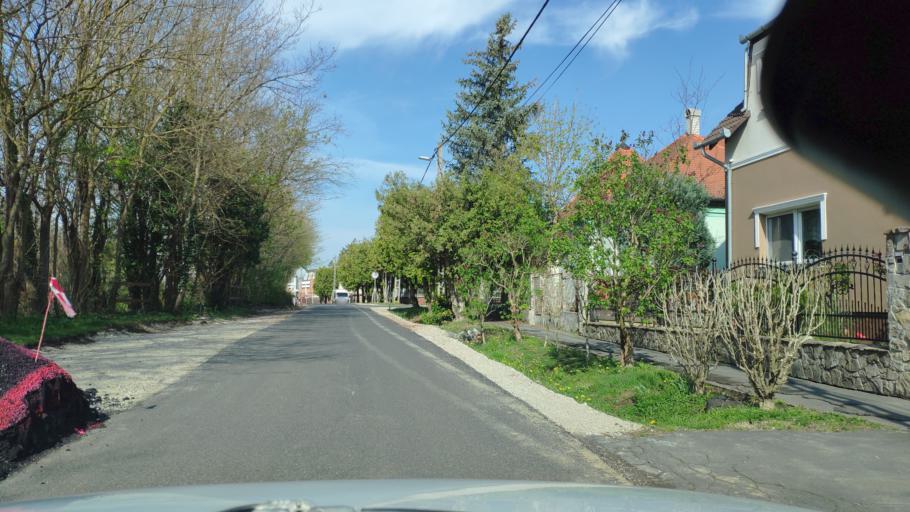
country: HU
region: Zala
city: Nagykanizsa
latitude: 46.4501
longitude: 17.0016
